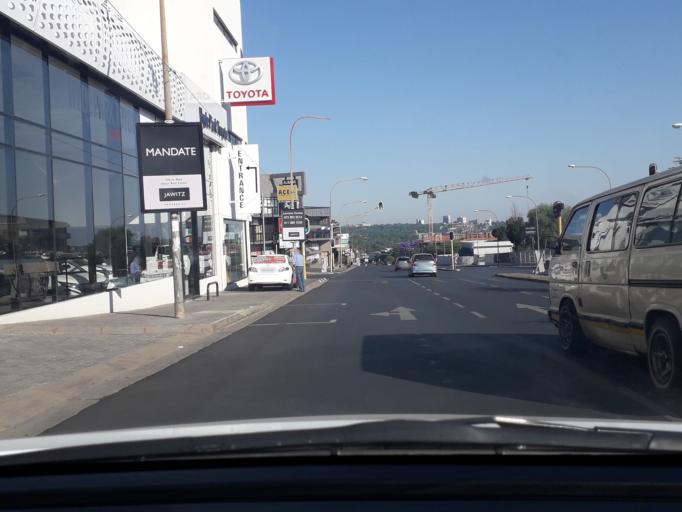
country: ZA
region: Gauteng
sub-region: City of Johannesburg Metropolitan Municipality
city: Johannesburg
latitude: -26.1202
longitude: 28.0280
